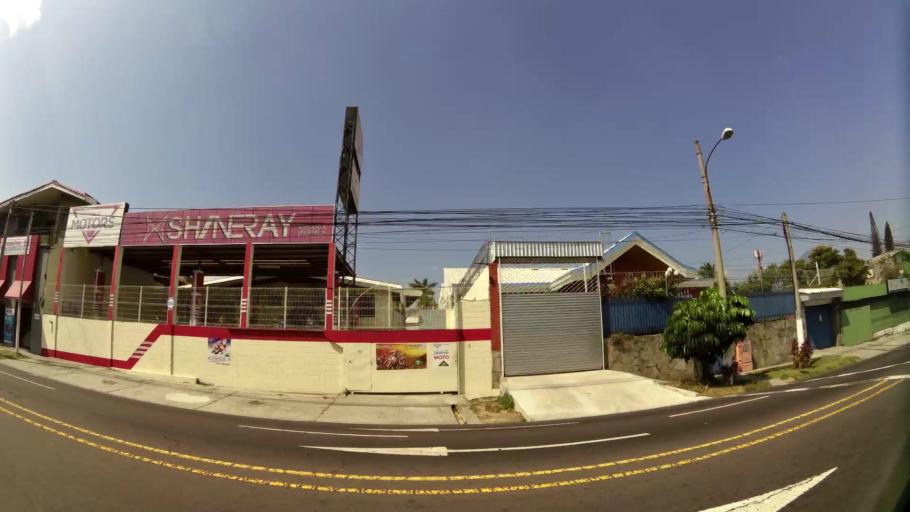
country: SV
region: San Salvador
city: San Salvador
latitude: 13.6862
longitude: -89.2227
